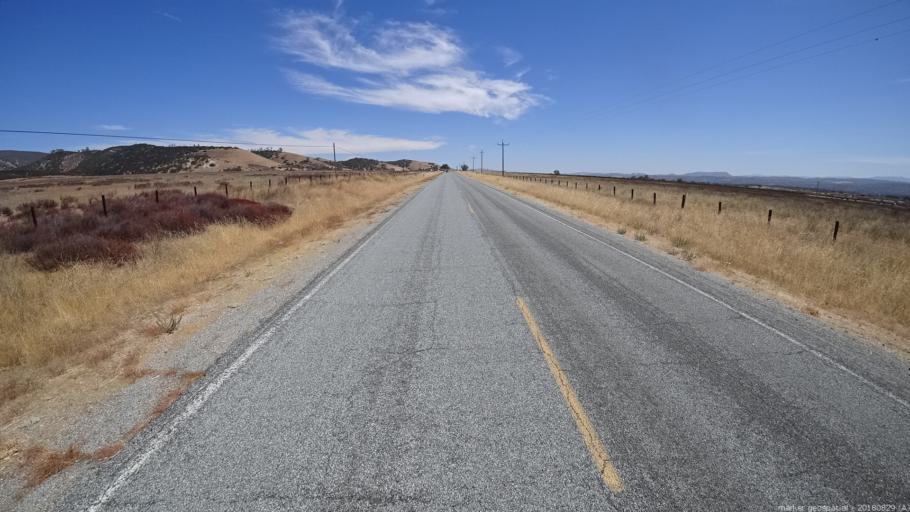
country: US
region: California
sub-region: San Luis Obispo County
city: Lake Nacimiento
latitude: 35.9257
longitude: -121.0434
